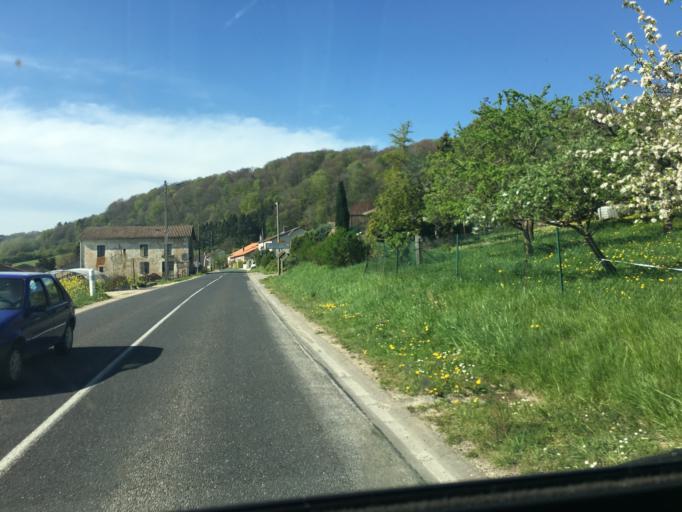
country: FR
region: Lorraine
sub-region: Departement de la Meuse
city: Vigneulles-les-Hattonchatel
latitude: 48.9086
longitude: 5.6657
